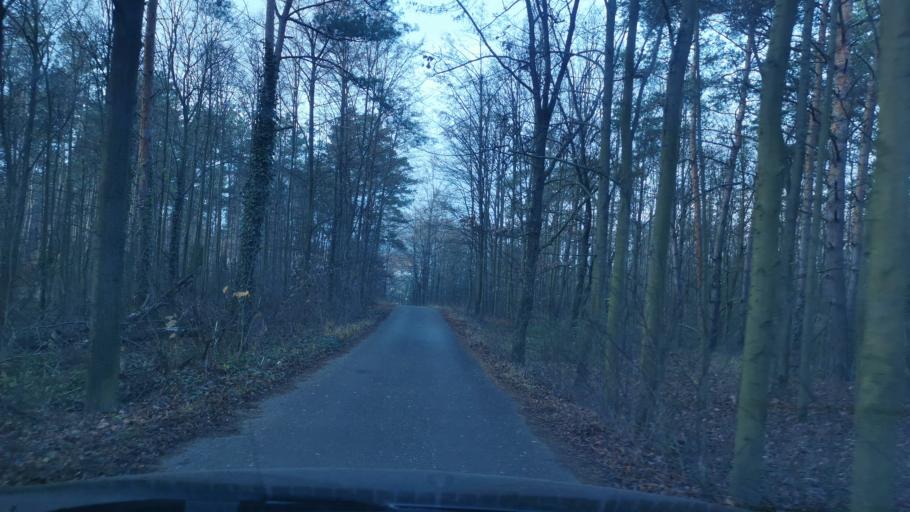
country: SK
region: Trnavsky
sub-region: Okres Skalica
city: Holic
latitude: 48.7990
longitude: 17.1713
